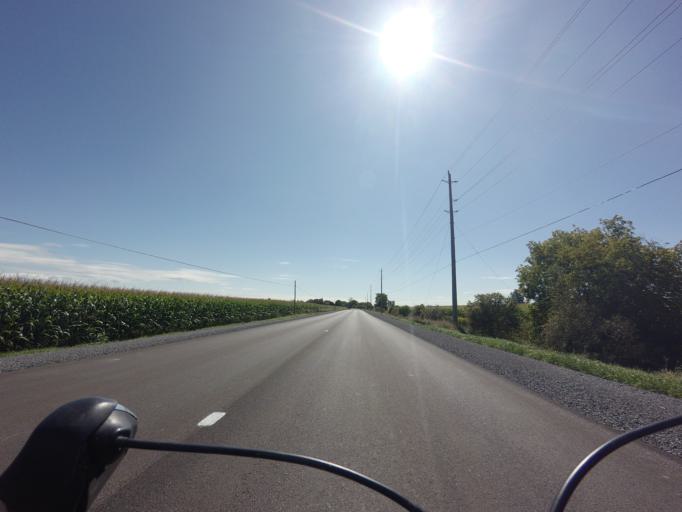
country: CA
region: Ontario
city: Bells Corners
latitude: 45.2214
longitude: -75.8542
